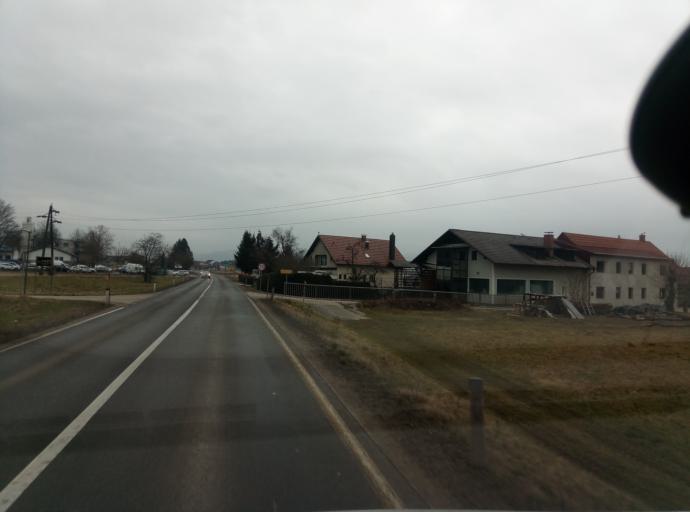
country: SI
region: Dol pri Ljubljani
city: Dol pri Ljubljani
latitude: 46.0917
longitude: 14.5714
